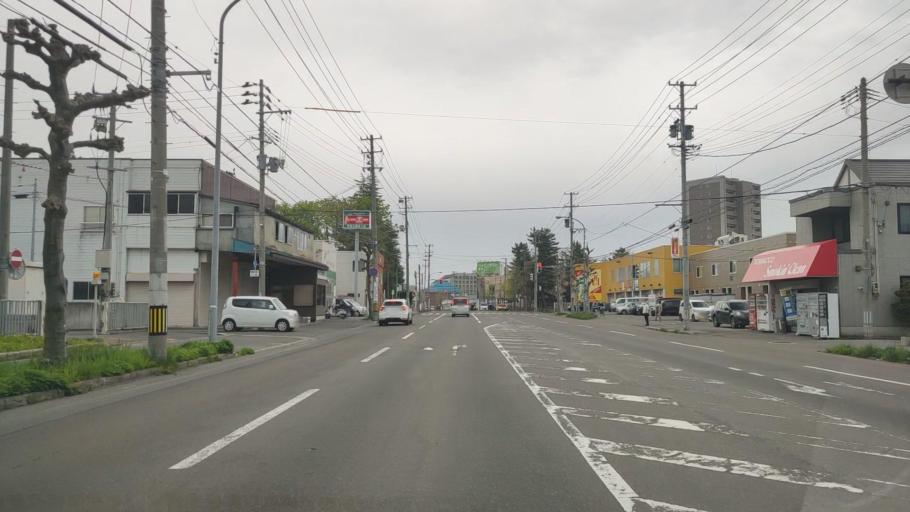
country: JP
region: Aomori
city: Aomori Shi
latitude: 40.8208
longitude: 140.7548
